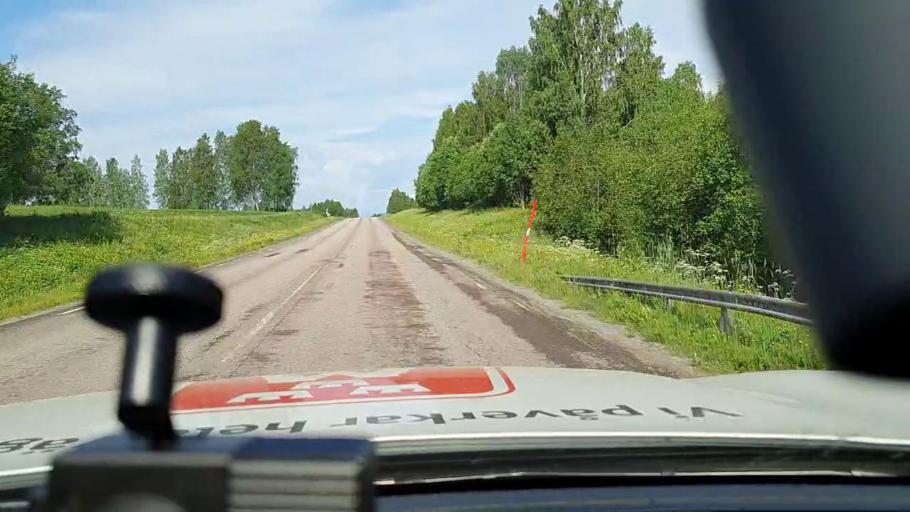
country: SE
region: Norrbotten
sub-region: Alvsbyns Kommun
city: AElvsbyn
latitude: 66.0141
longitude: 21.1661
